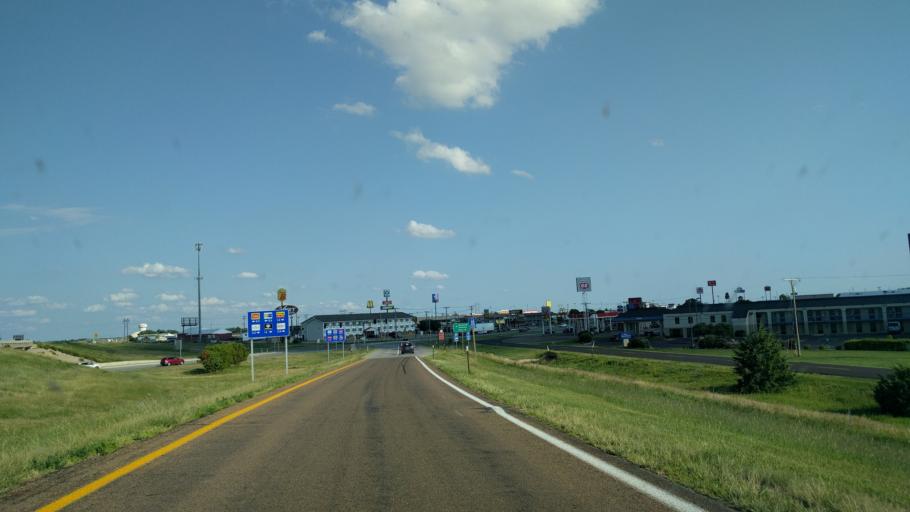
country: US
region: Kansas
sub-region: Ellis County
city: Hays
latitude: 38.8987
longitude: -99.3194
